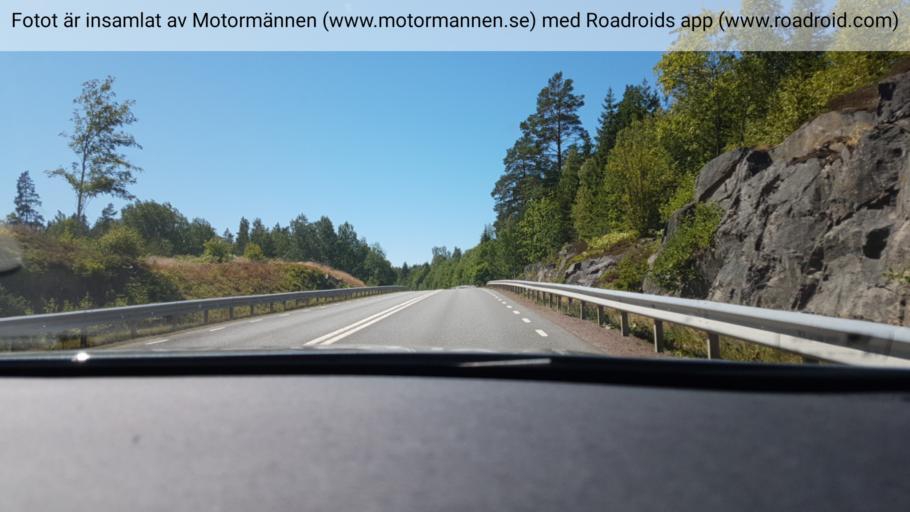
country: SE
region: Joenkoeping
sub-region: Jonkopings Kommun
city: Asa
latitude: 58.0120
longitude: 14.6518
